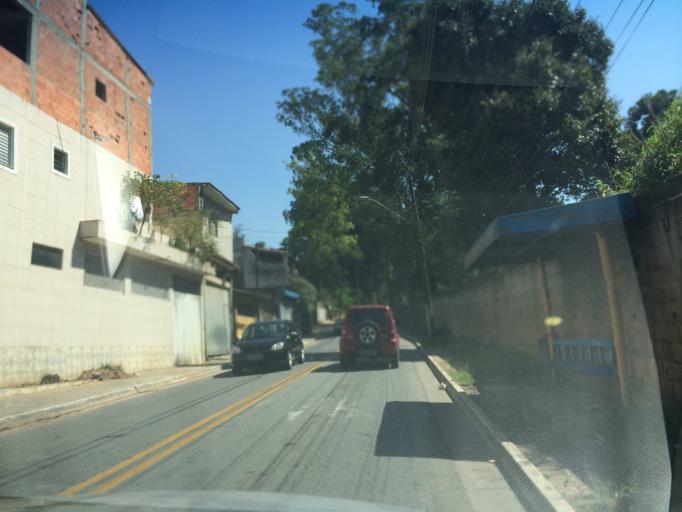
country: BR
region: Sao Paulo
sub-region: Guarulhos
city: Guarulhos
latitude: -23.4221
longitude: -46.5423
